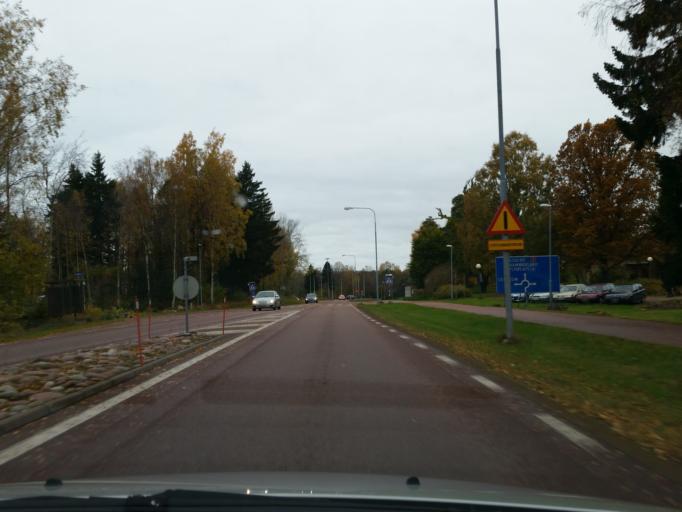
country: AX
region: Mariehamns stad
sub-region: Mariehamn
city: Mariehamn
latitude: 60.1140
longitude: 19.9343
